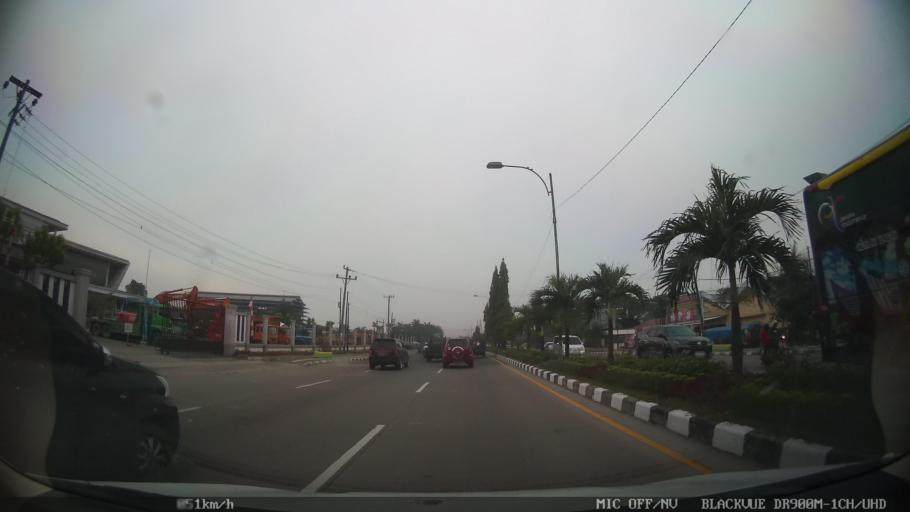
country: ID
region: North Sumatra
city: Deli Tua
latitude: 3.5371
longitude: 98.7124
